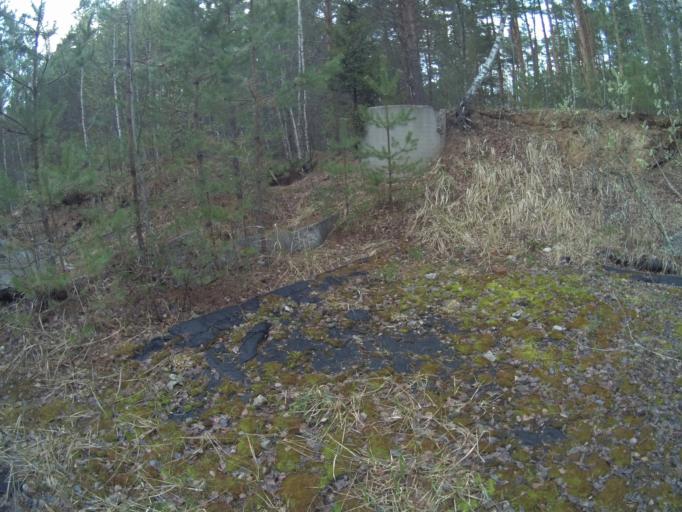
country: RU
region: Vladimir
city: Raduzhnyy
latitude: 56.0376
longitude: 40.3665
